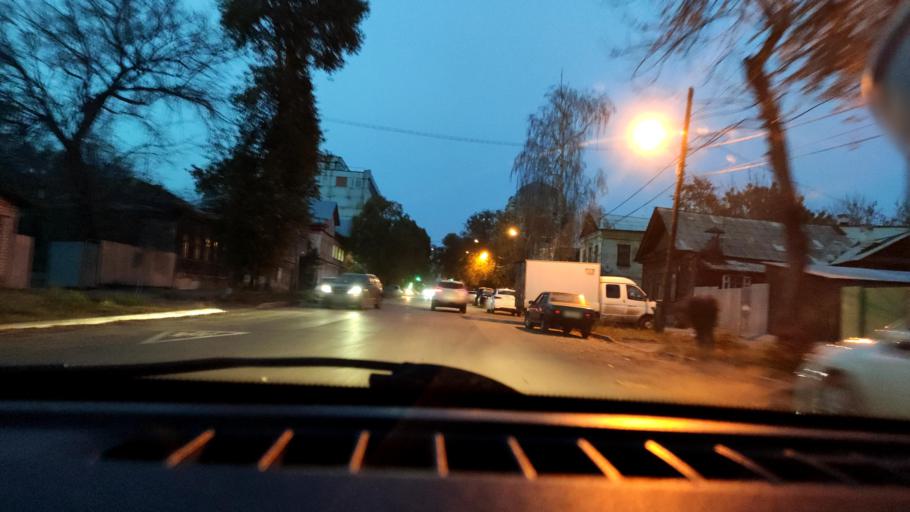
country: RU
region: Samara
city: Samara
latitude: 53.1829
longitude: 50.1011
